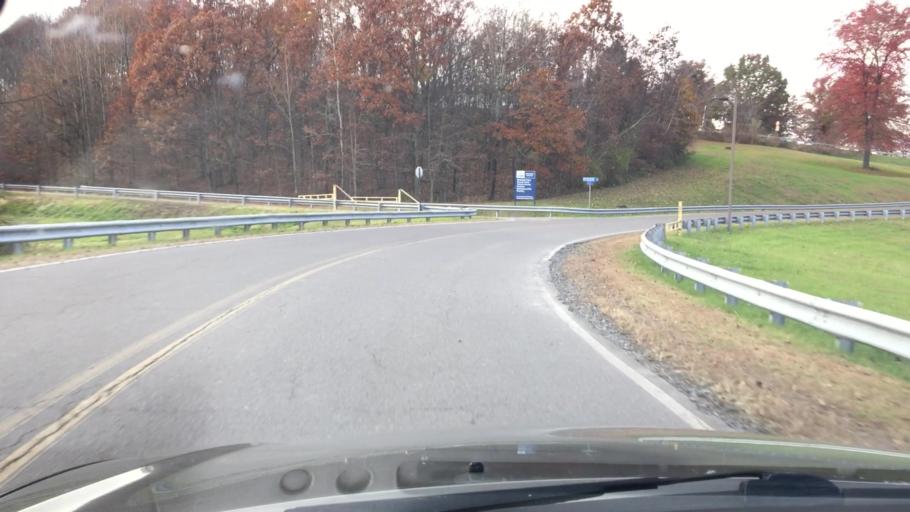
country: US
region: Pennsylvania
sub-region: Luzerne County
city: Nanticoke
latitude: 41.1944
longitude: -75.9883
